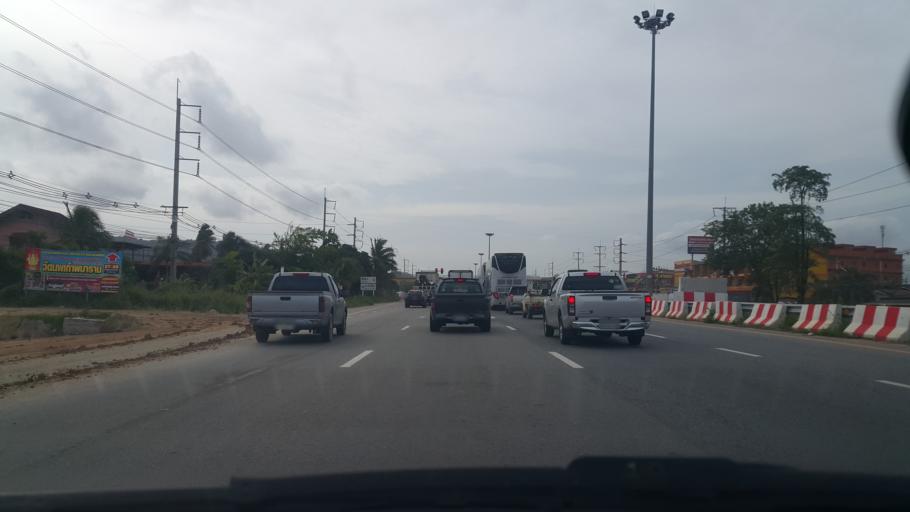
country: TH
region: Rayong
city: Nikhom Phattana
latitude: 12.8107
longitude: 101.1413
